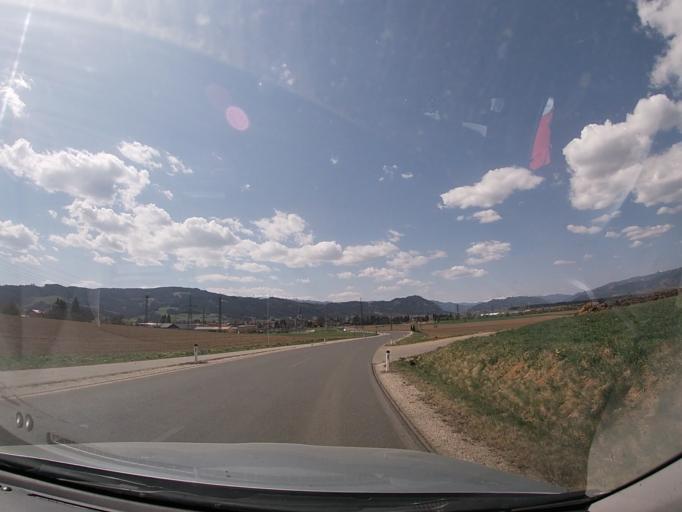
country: AT
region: Styria
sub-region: Politischer Bezirk Murtal
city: Weisskirchen in Steiermark
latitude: 47.1564
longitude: 14.7519
